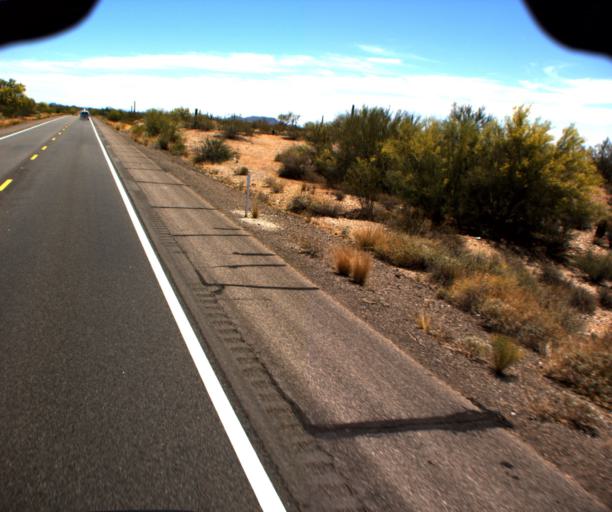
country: US
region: Arizona
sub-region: Maricopa County
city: Sun City West
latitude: 33.8418
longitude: -112.5005
